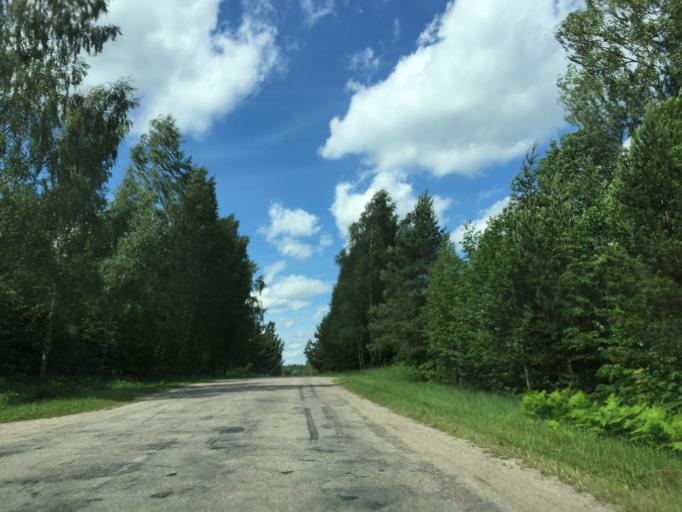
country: LV
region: Engure
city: Smarde
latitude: 56.9717
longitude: 23.3212
